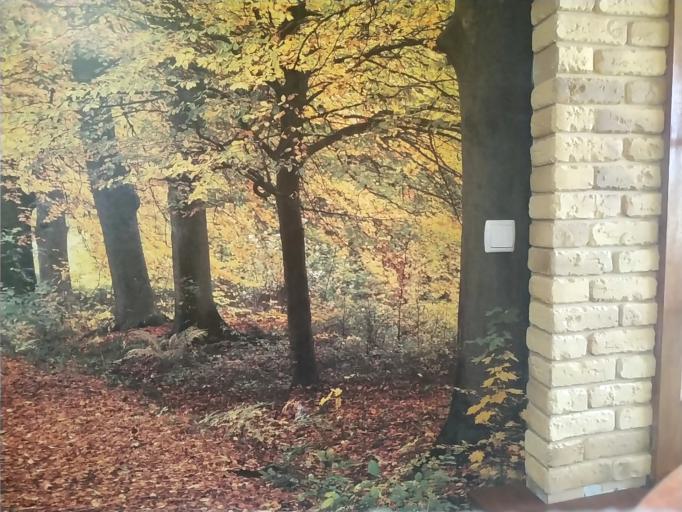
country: RU
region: Tverskaya
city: Vyshniy Volochek
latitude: 57.6507
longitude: 34.5515
